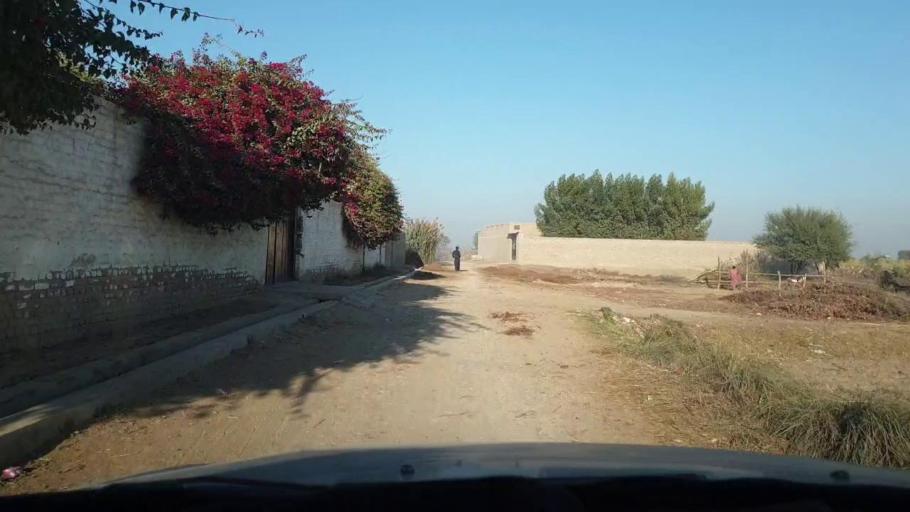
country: PK
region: Sindh
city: Adilpur
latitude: 27.9544
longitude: 69.2317
